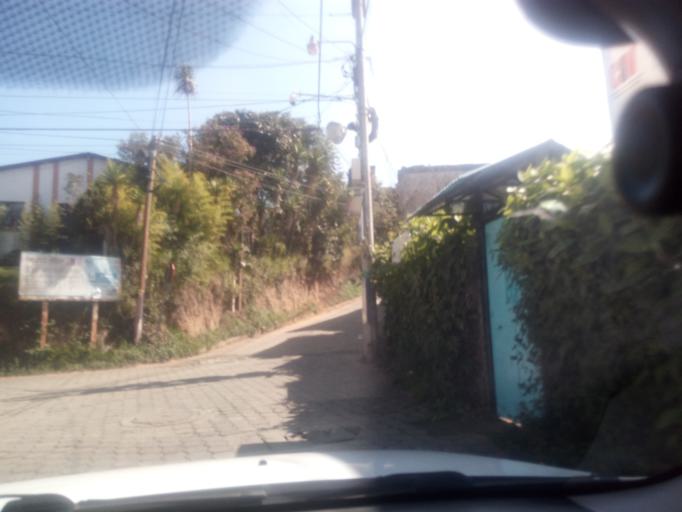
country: GT
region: Sacatepequez
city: San Bartolome Milpas Altas
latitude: 14.6040
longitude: -90.6773
